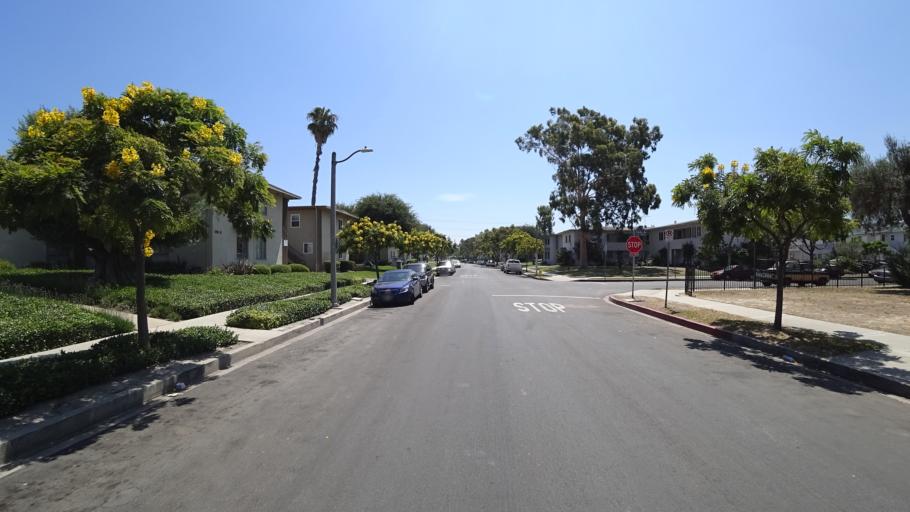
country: US
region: California
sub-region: Los Angeles County
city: Culver City
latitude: 34.0249
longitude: -118.3692
